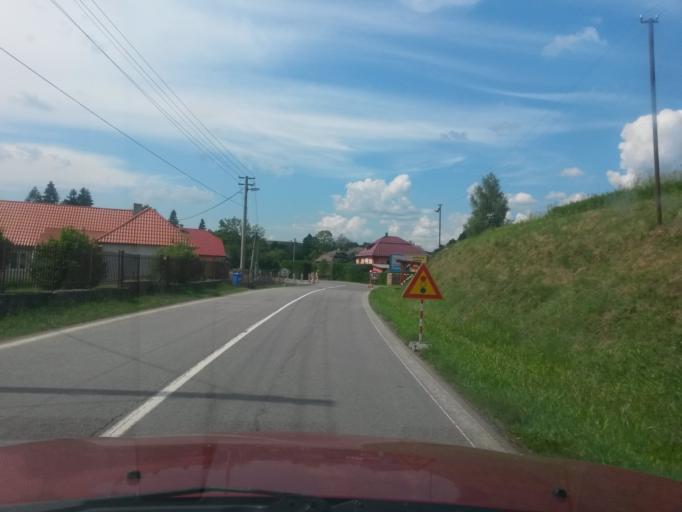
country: UA
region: Zakarpattia
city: Velykyi Bereznyi
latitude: 48.9020
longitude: 22.3860
